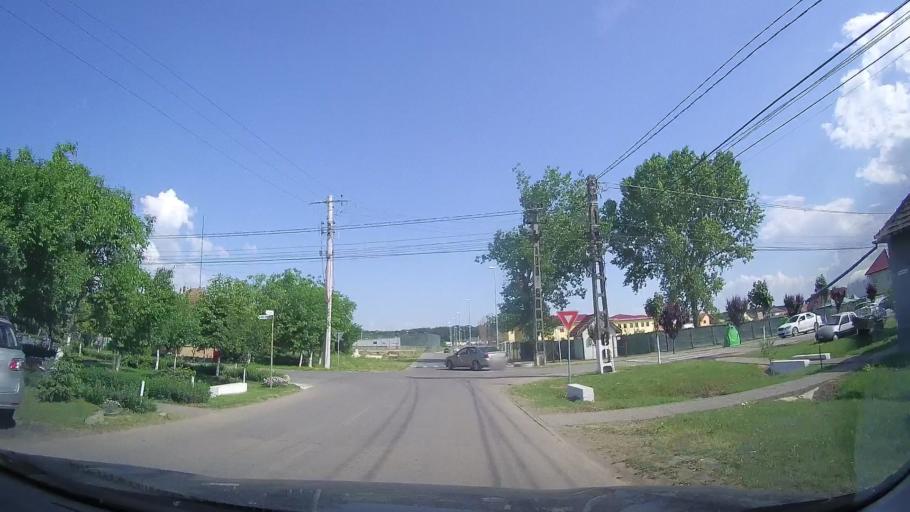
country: RO
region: Timis
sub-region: Comuna Dumbravita
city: Dumbravita
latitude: 45.8002
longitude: 21.2495
